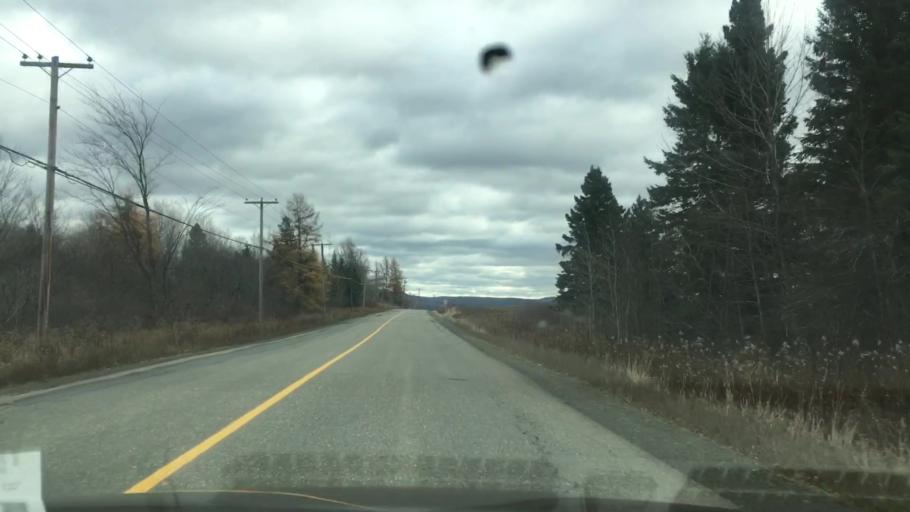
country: US
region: Maine
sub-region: Aroostook County
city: Fort Fairfield
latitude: 46.7555
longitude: -67.7632
